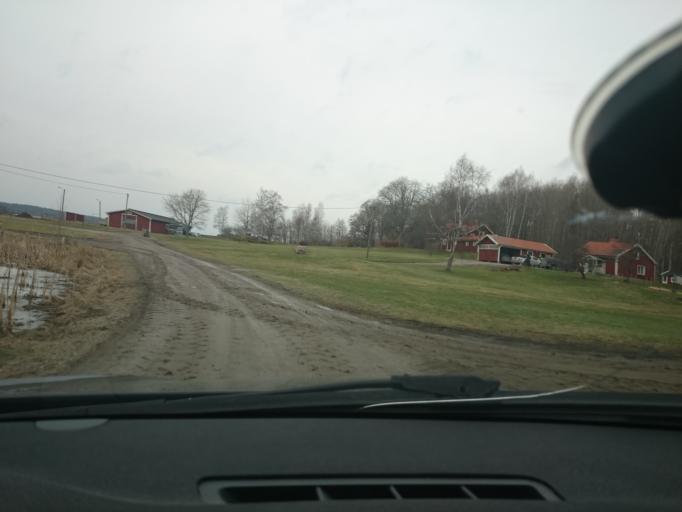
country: SE
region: OEstergoetland
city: Lindo
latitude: 58.5632
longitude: 16.2591
